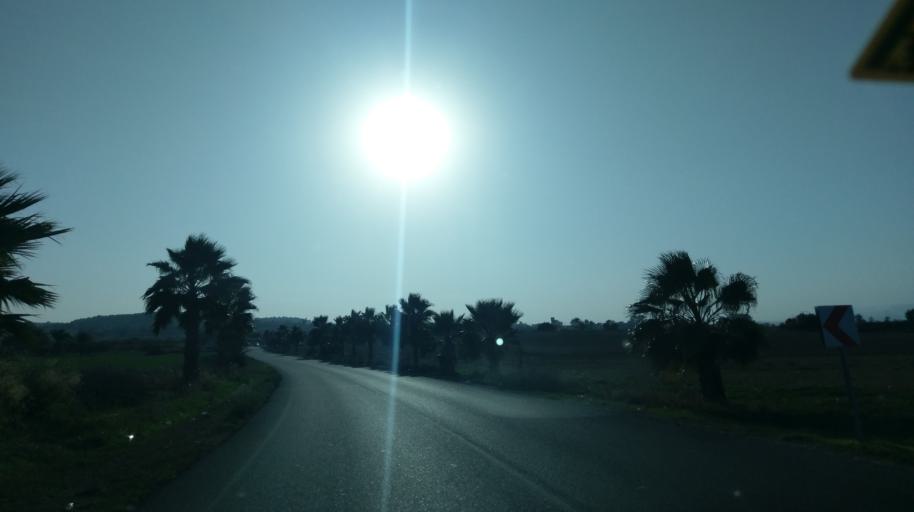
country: CY
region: Ammochostos
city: Leonarisso
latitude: 35.3734
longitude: 34.0391
